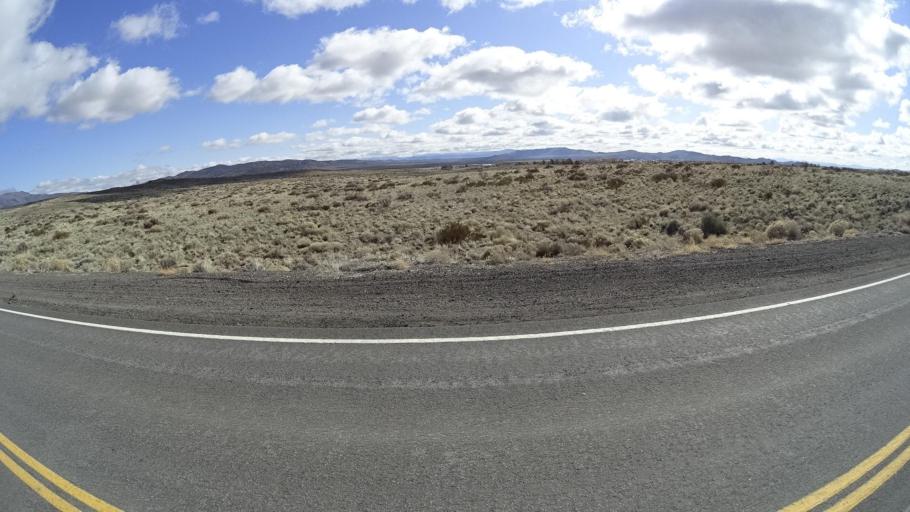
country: US
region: Nevada
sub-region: Washoe County
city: Cold Springs
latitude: 39.6754
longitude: -119.9225
